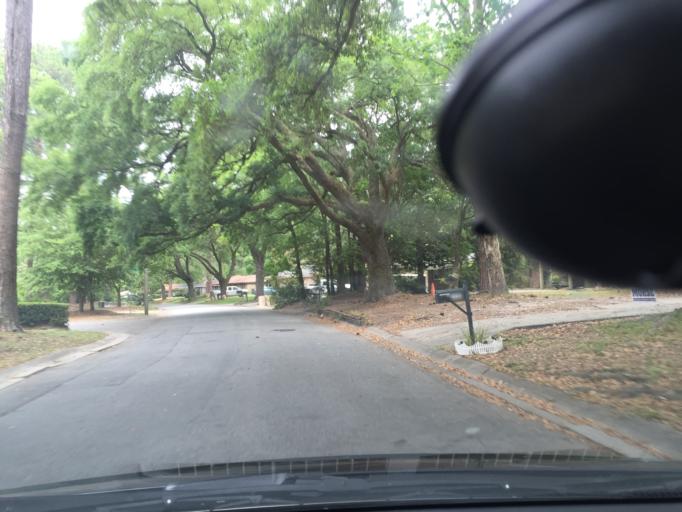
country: US
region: Georgia
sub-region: Chatham County
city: Montgomery
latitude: 31.9905
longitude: -81.1234
